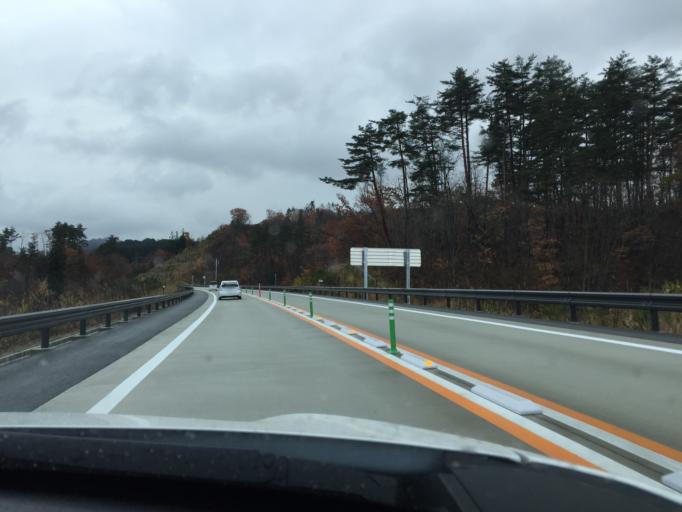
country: JP
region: Yamagata
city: Yonezawa
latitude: 37.8847
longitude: 140.1741
